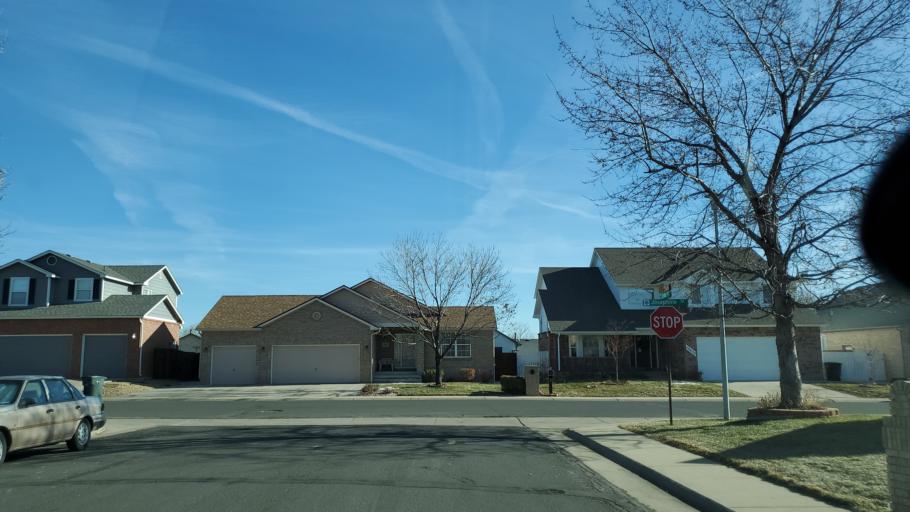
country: US
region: Colorado
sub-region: Adams County
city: Northglenn
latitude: 39.9228
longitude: -104.9578
